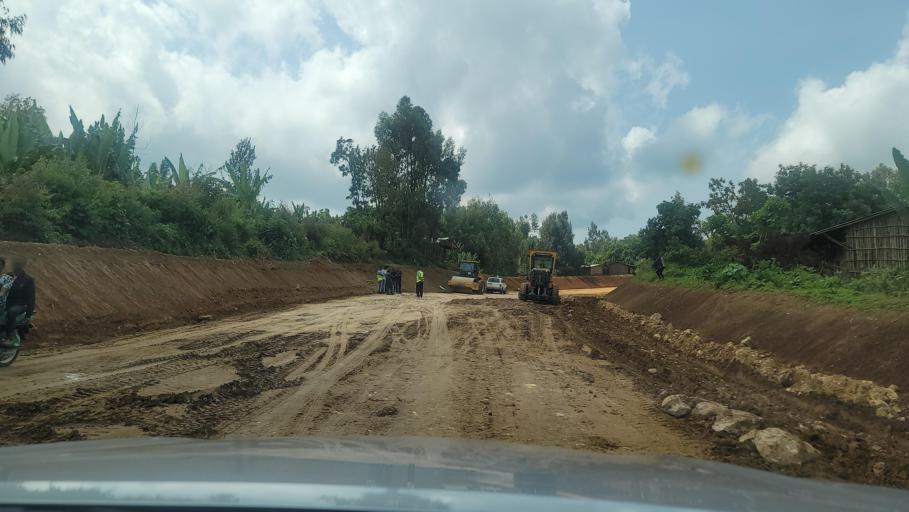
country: ET
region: Oromiya
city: Agaro
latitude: 7.8024
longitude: 36.4568
